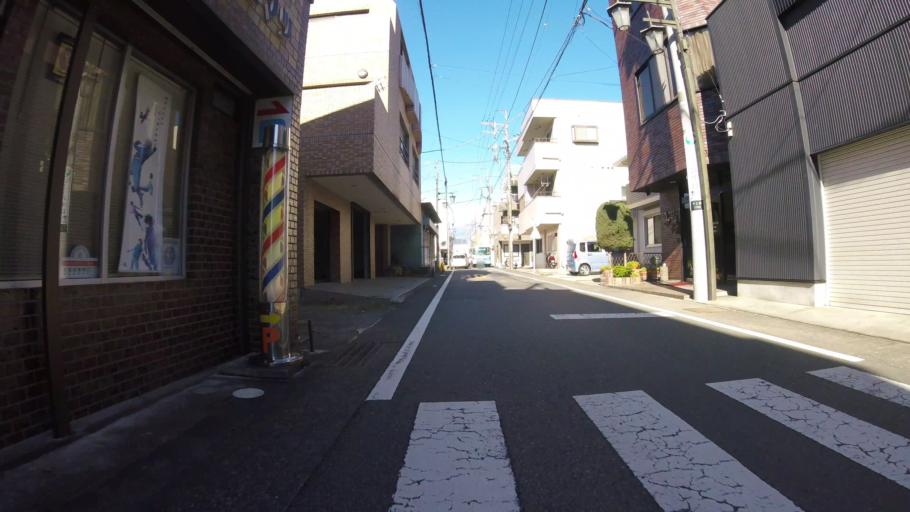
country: JP
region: Shizuoka
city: Mishima
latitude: 35.1302
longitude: 138.8957
